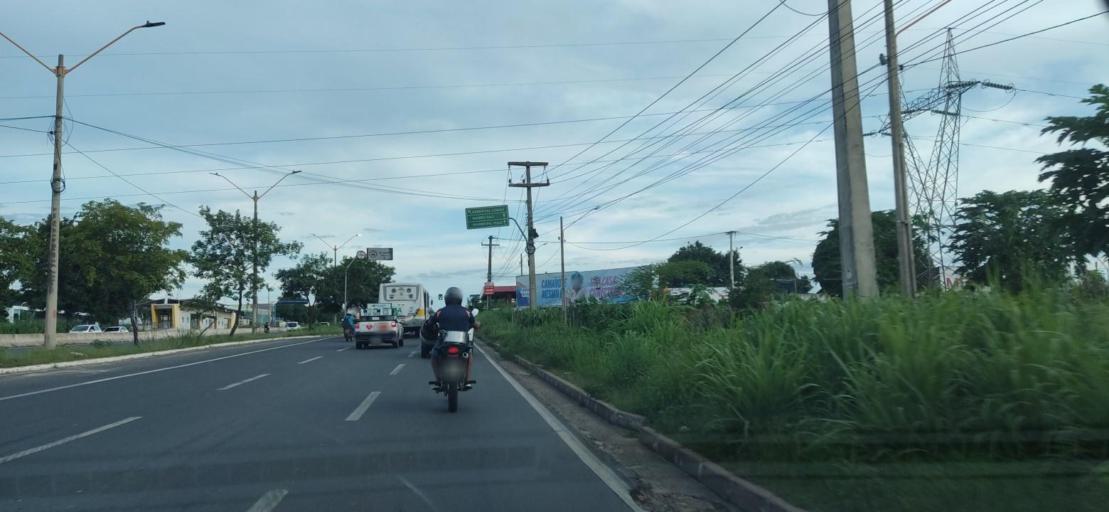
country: BR
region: Piaui
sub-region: Teresina
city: Teresina
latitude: -5.1252
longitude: -42.7947
